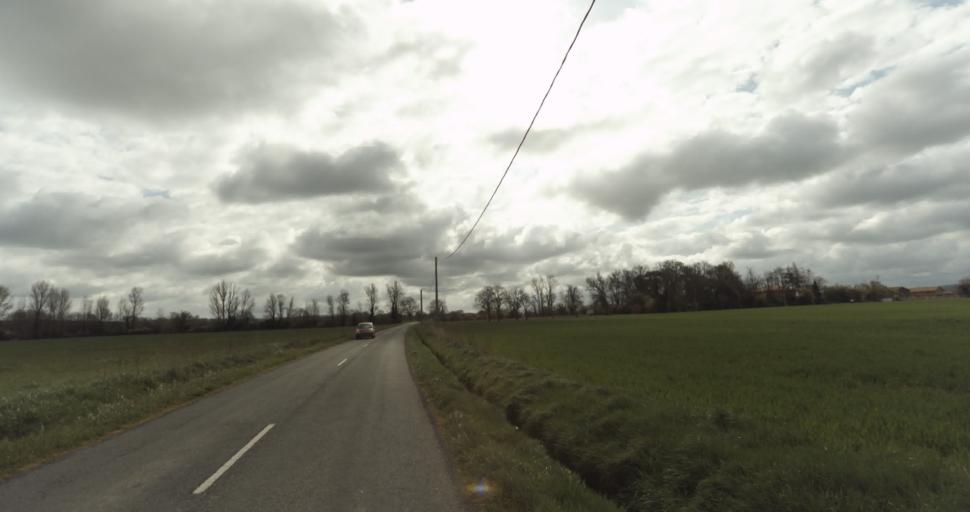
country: FR
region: Midi-Pyrenees
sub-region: Departement de la Haute-Garonne
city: Miremont
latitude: 43.3621
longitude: 1.4433
